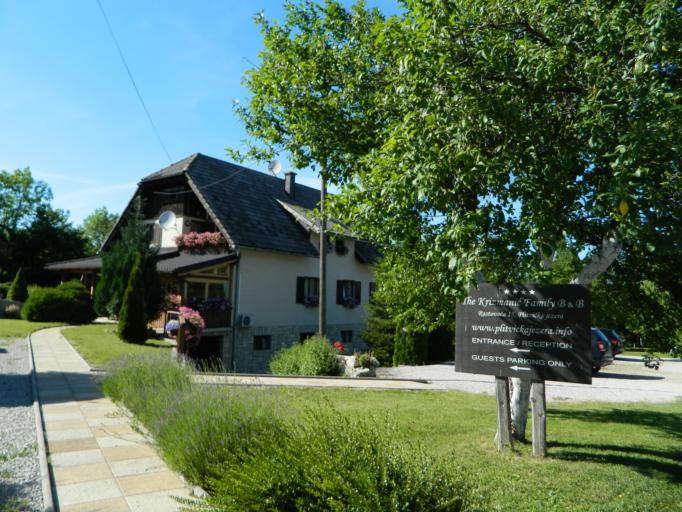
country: HR
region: Licko-Senjska
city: Jezerce
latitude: 44.9113
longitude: 15.6140
